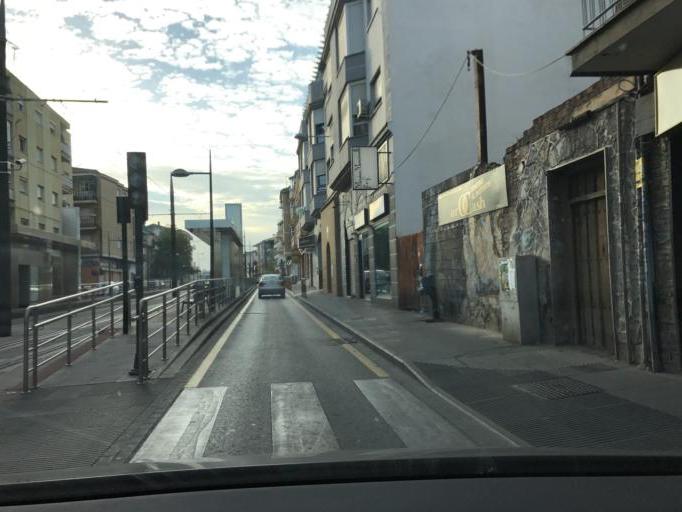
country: ES
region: Andalusia
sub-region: Provincia de Granada
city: Maracena
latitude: 37.2074
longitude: -3.6307
